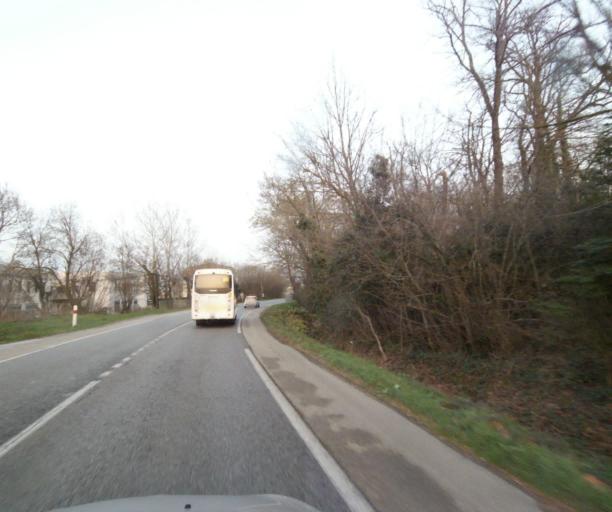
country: FR
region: Provence-Alpes-Cote d'Azur
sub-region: Departement des Bouches-du-Rhone
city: Cabries
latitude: 43.4256
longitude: 5.3842
